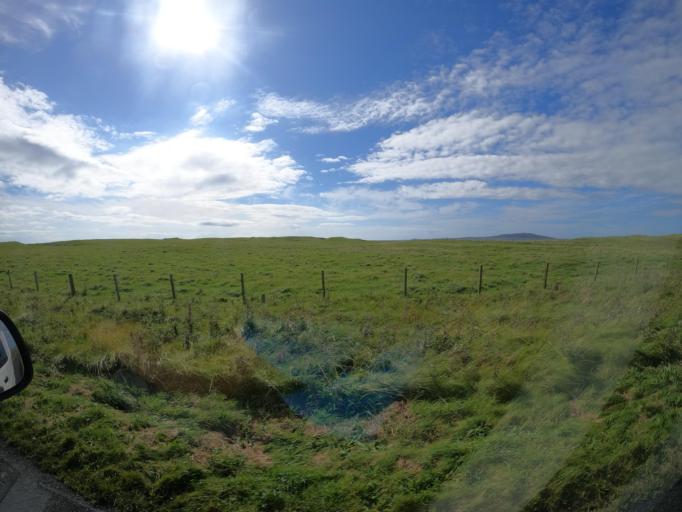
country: GB
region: Scotland
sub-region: Eilean Siar
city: Barra
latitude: 56.4932
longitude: -6.8465
